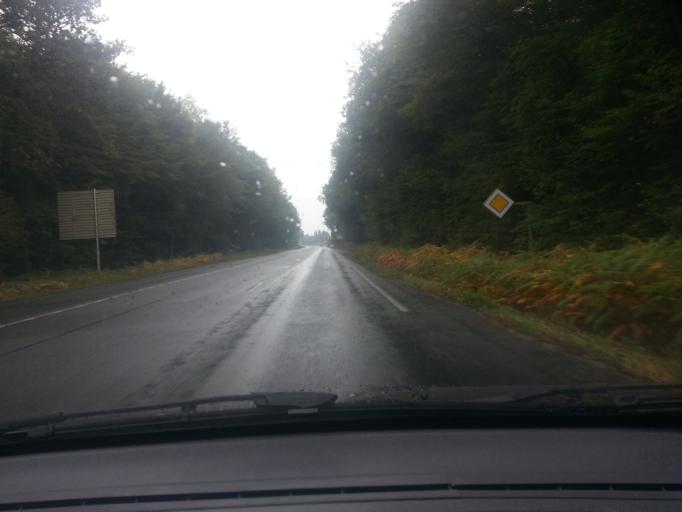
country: FR
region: Bourgogne
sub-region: Departement de Saone-et-Loire
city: Montchanin
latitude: 46.7544
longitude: 4.4851
